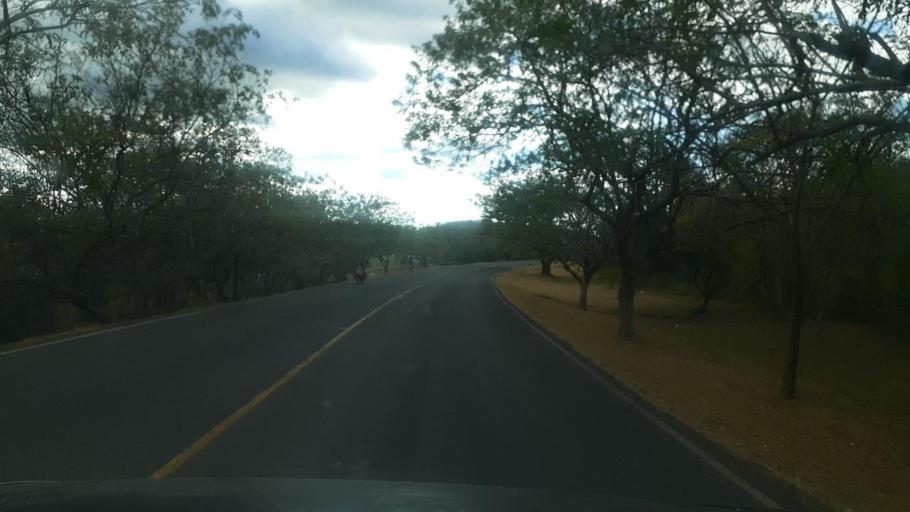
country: NI
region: Madriz
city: Somoto
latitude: 13.4705
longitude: -86.6051
